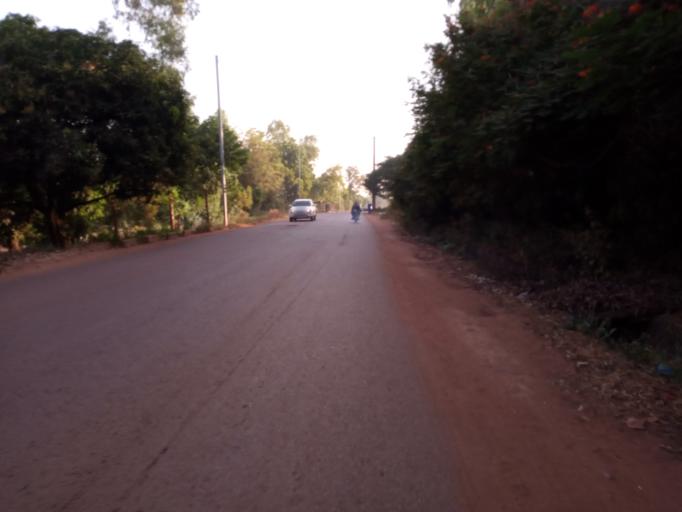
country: ML
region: Bamako
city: Bamako
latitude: 12.6311
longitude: -7.9435
